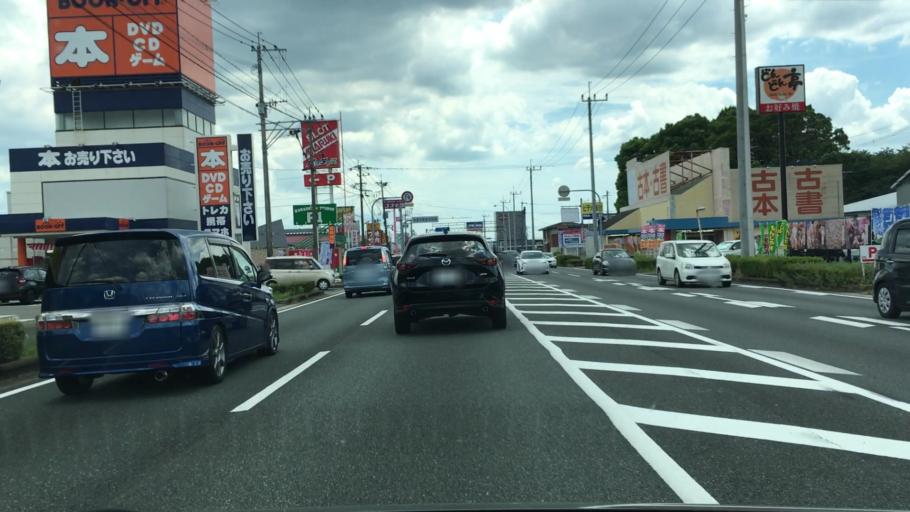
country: JP
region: Saga Prefecture
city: Tosu
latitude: 33.3833
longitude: 130.4993
